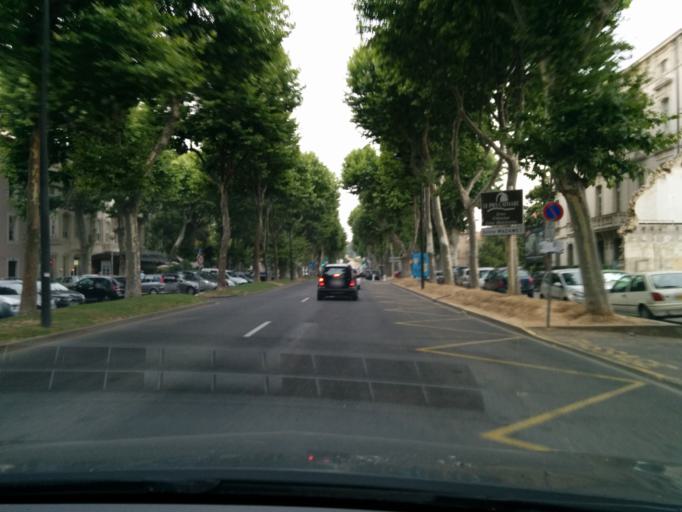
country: FR
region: Languedoc-Roussillon
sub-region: Departement de l'Aude
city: Carcassonne
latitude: 43.2136
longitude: 2.3555
